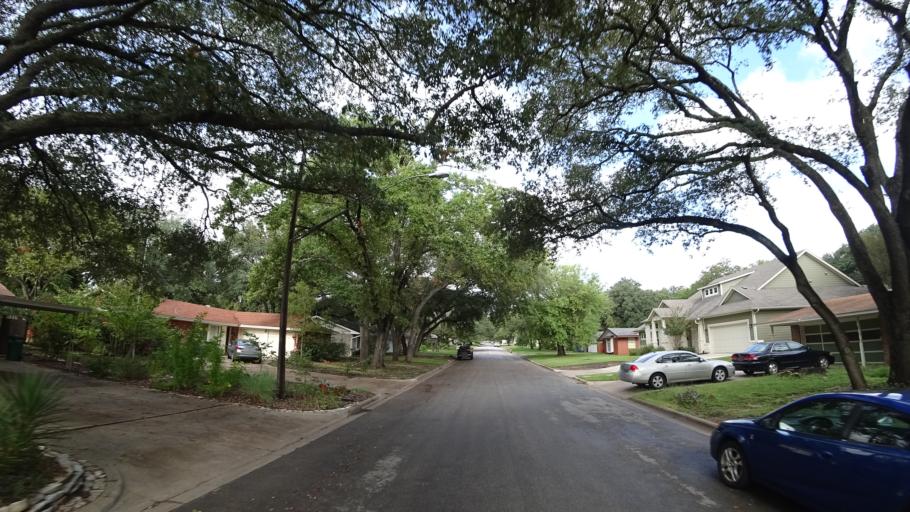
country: US
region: Texas
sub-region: Travis County
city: West Lake Hills
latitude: 30.3531
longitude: -97.7435
